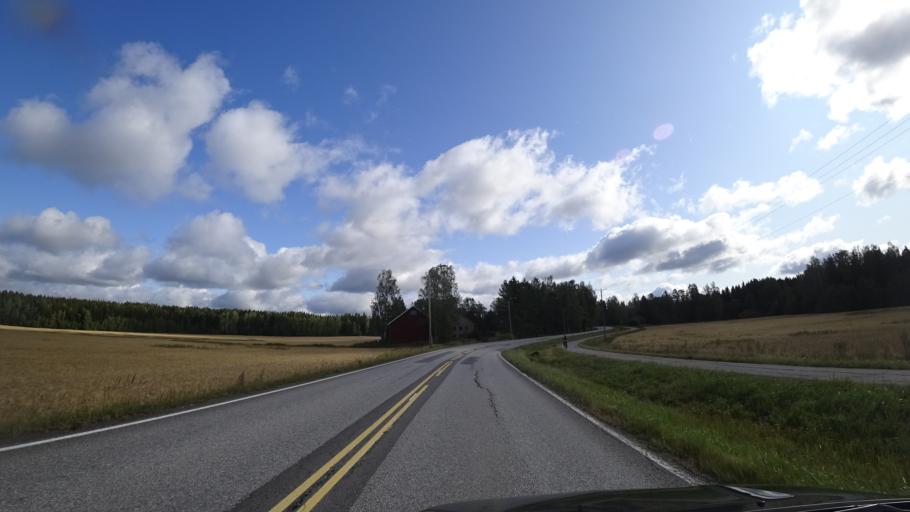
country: FI
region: Uusimaa
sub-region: Helsinki
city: Hyvinge
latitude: 60.5765
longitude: 24.9832
